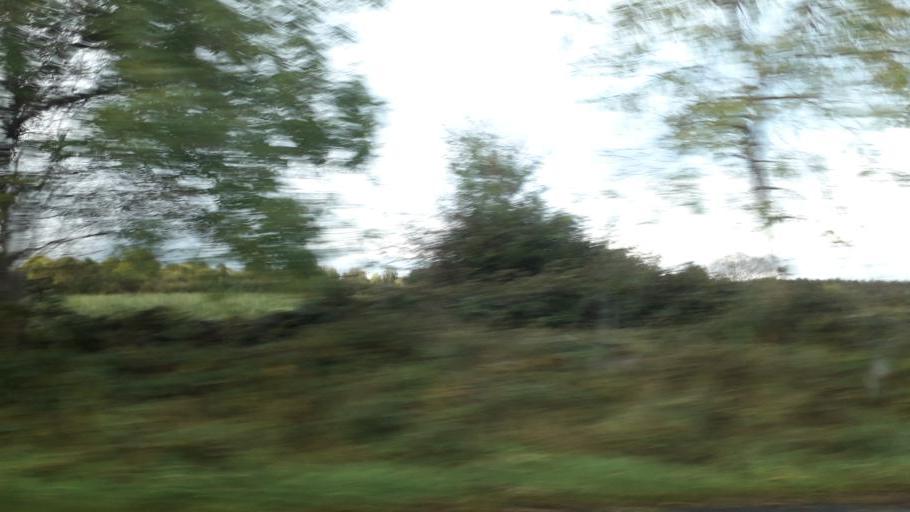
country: IE
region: Leinster
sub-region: An Longfort
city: Lanesborough
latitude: 53.7483
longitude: -7.9458
